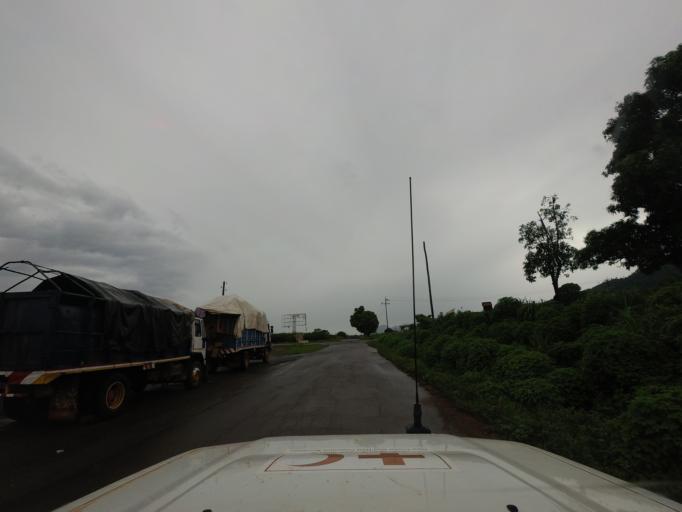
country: LR
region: Nimba
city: New Yekepa
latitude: 7.5665
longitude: -8.5450
